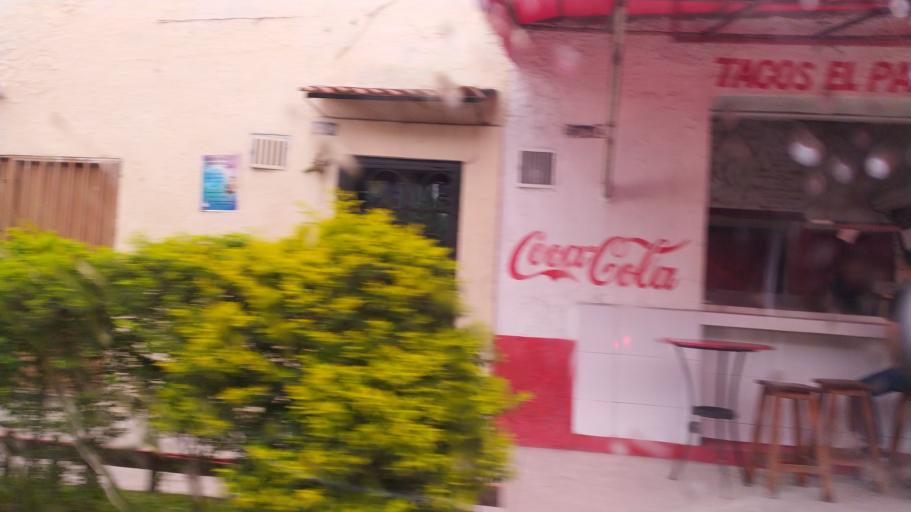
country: MX
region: Jalisco
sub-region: Zapopan
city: Zapopan
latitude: 20.7170
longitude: -103.3660
